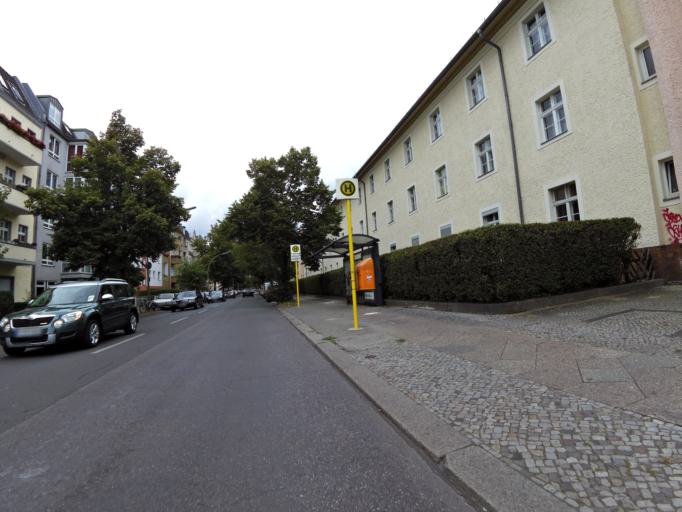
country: DE
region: Berlin
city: Mariendorf
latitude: 52.4452
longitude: 13.3739
